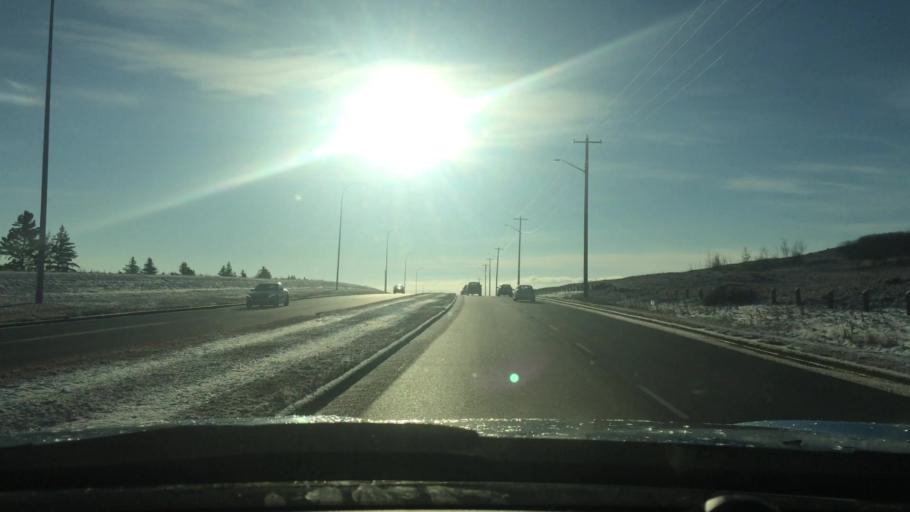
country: CA
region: Alberta
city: Calgary
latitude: 51.1220
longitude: -114.0928
